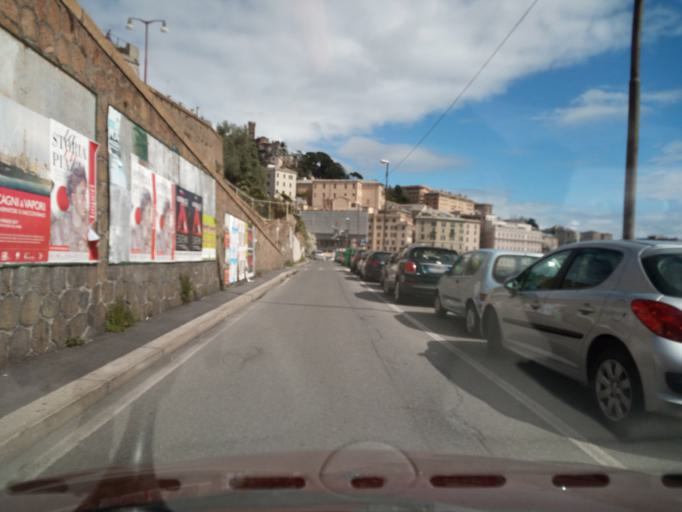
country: IT
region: Liguria
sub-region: Provincia di Genova
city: Genoa
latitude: 44.4179
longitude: 8.9196
